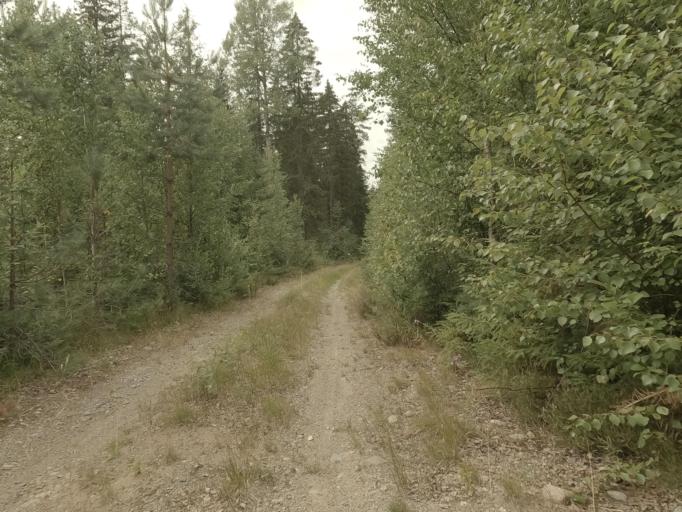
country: RU
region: Leningrad
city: Kamennogorsk
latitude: 61.0206
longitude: 29.1727
